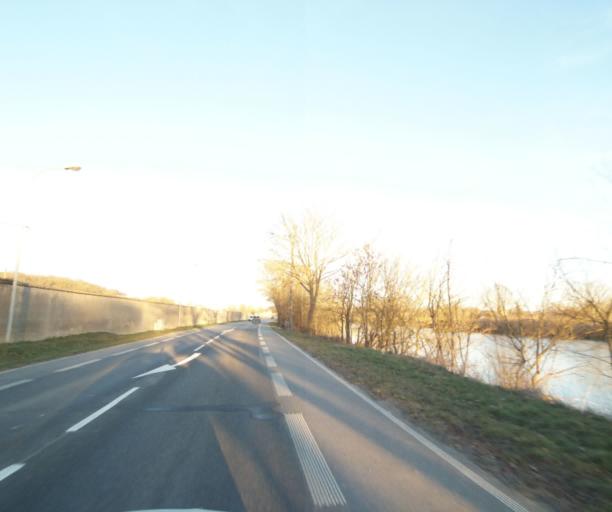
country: FR
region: Lorraine
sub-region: Departement de Meurthe-et-Moselle
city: Laneuveville-devant-Nancy
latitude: 48.6617
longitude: 6.2438
